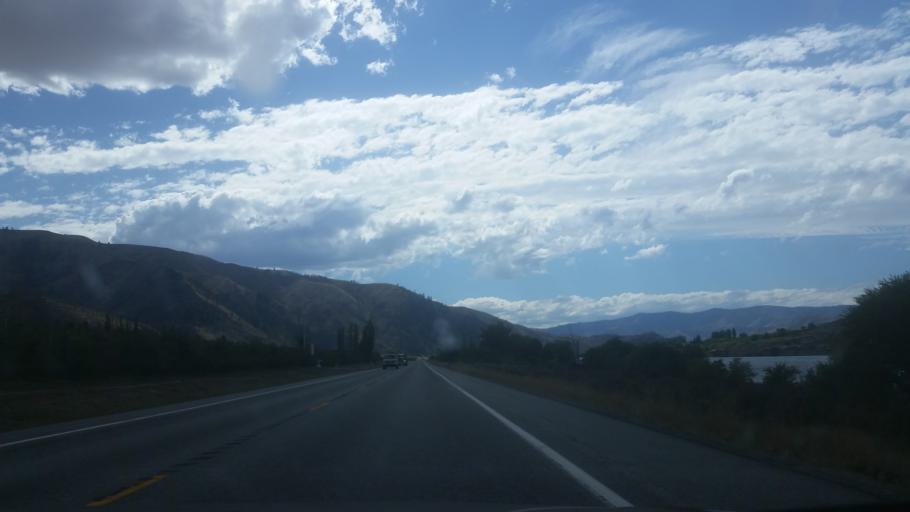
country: US
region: Washington
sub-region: Chelan County
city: Chelan
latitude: 47.7711
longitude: -120.0465
